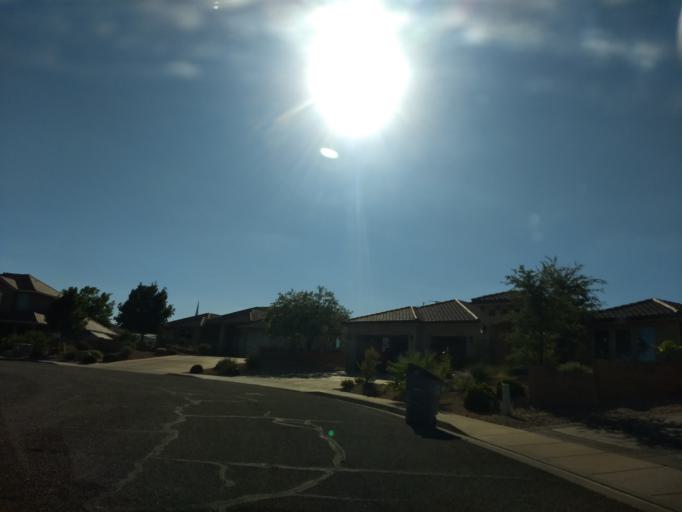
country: US
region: Utah
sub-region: Washington County
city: Saint George
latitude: 37.0933
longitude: -113.5456
